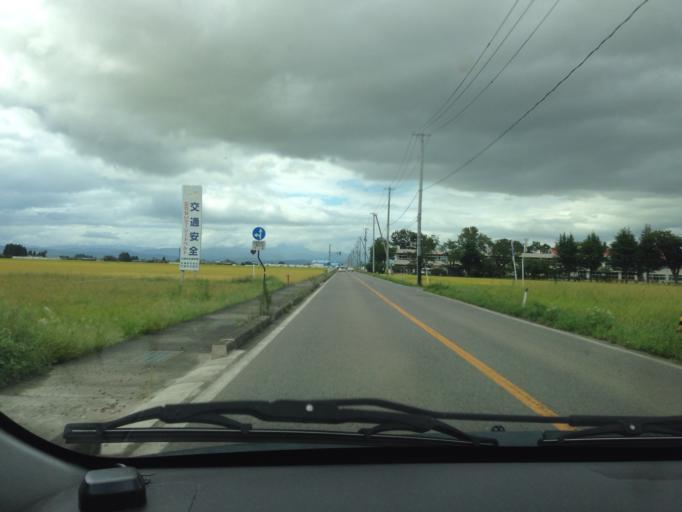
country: JP
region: Fukushima
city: Kitakata
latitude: 37.4634
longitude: 139.8803
